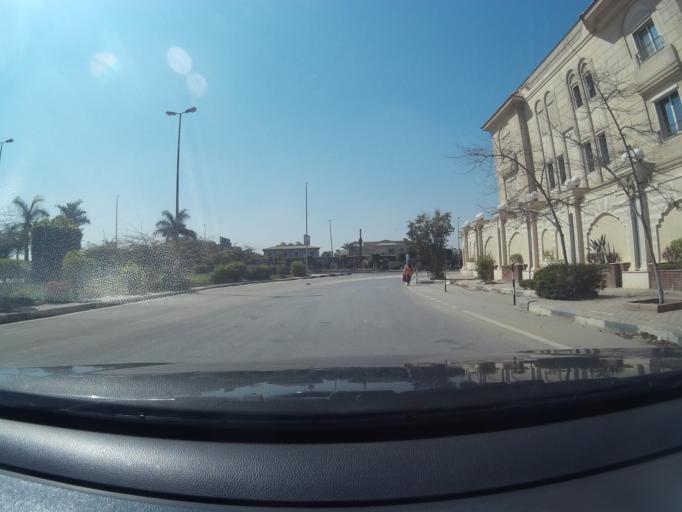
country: EG
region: Muhafazat al Qahirah
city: Cairo
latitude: 30.0050
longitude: 31.4040
